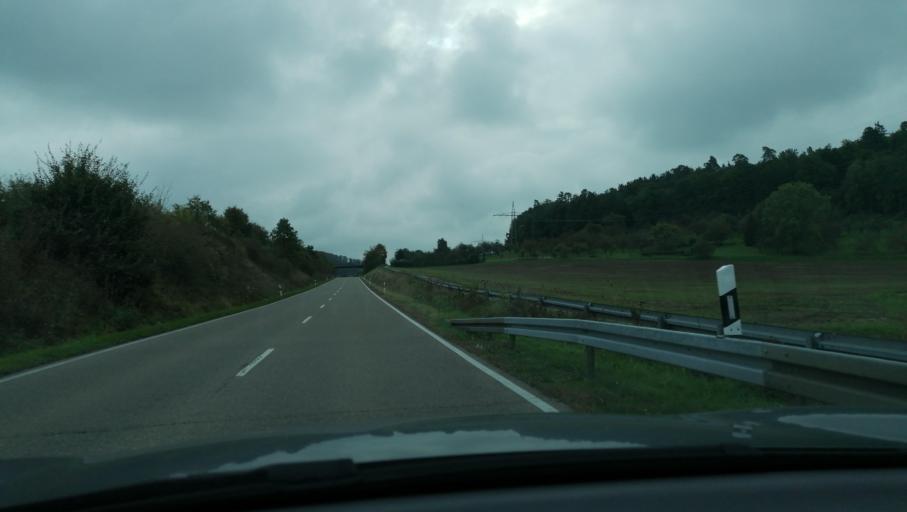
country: DE
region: Baden-Wuerttemberg
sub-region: Regierungsbezirk Stuttgart
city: Winnenden
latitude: 48.8613
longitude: 9.4274
